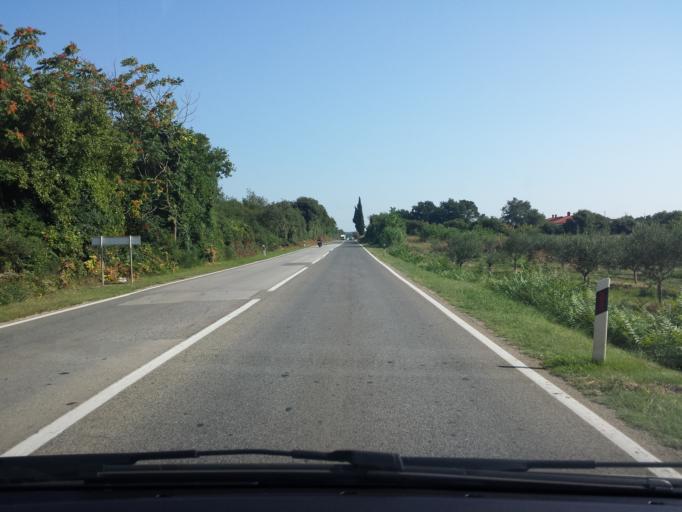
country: HR
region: Istarska
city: Galizana
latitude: 44.9088
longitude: 13.8477
